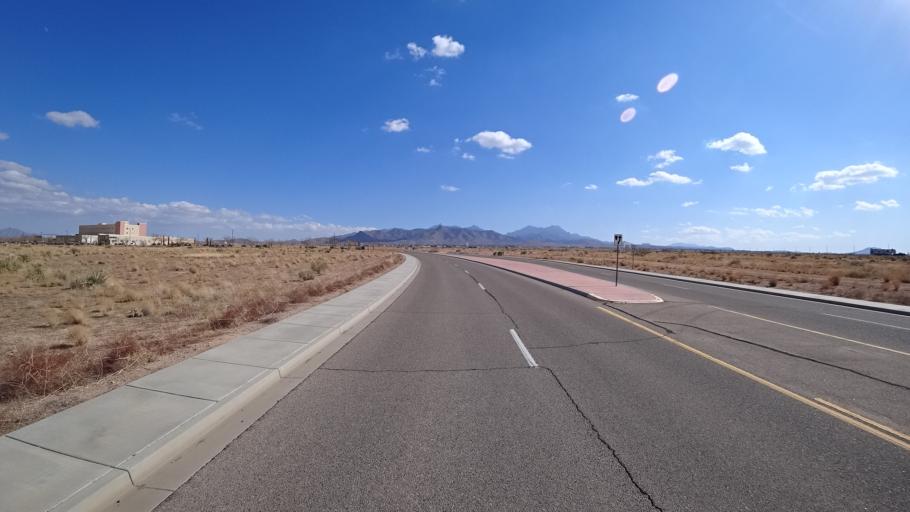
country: US
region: Arizona
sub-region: Mohave County
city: New Kingman-Butler
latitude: 35.2190
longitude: -113.9905
